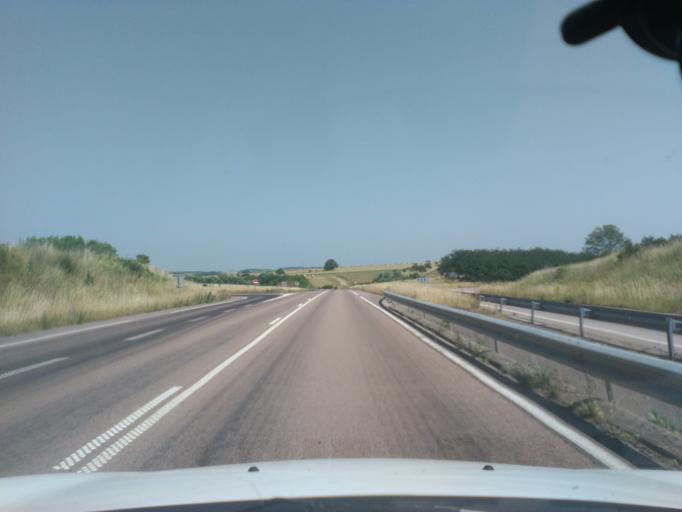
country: FR
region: Lorraine
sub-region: Departement des Vosges
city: Chatenois
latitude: 48.3057
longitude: 5.9337
